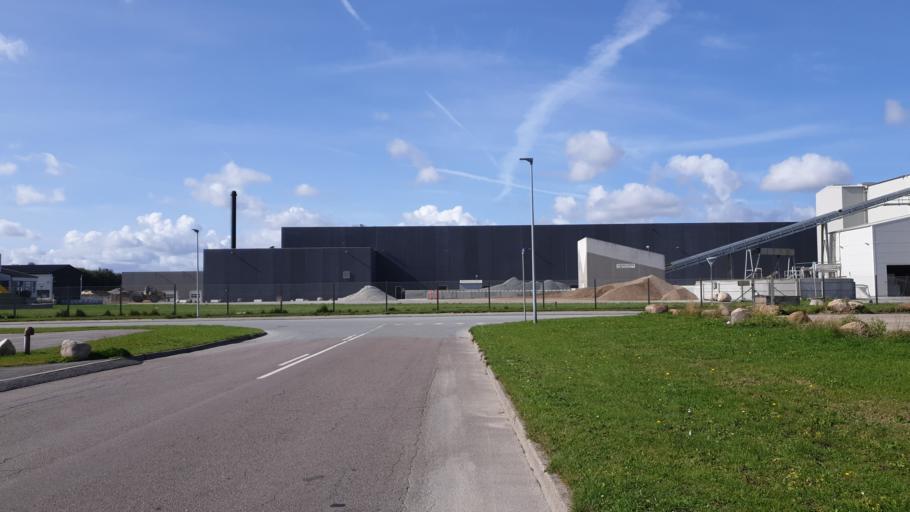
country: DK
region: Central Jutland
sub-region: Hedensted Kommune
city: Hedensted
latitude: 55.8090
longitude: 9.6866
